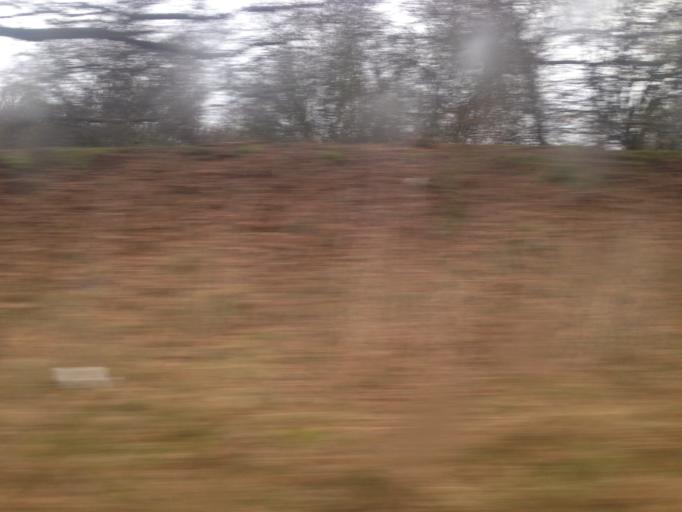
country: GB
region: England
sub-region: Greater London
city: Mitcham
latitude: 51.3914
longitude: -0.1536
